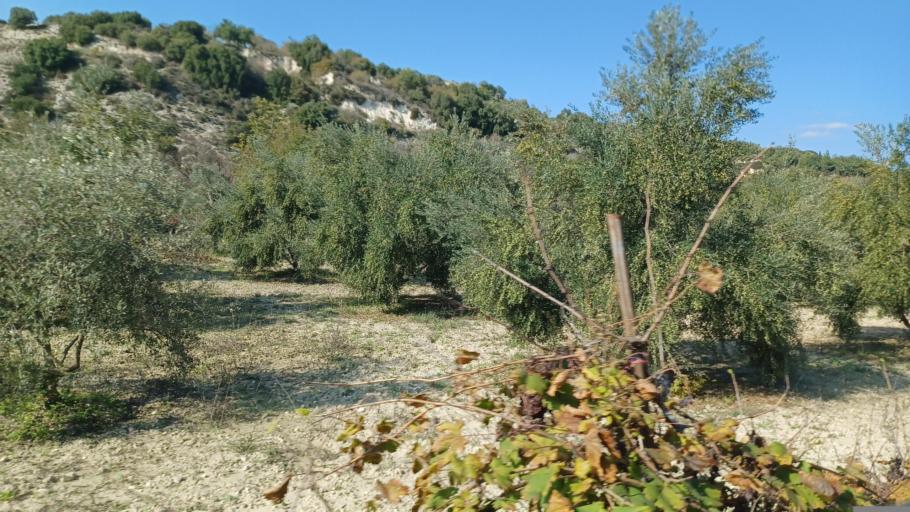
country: CY
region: Pafos
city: Mesogi
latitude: 34.8526
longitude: 32.5116
